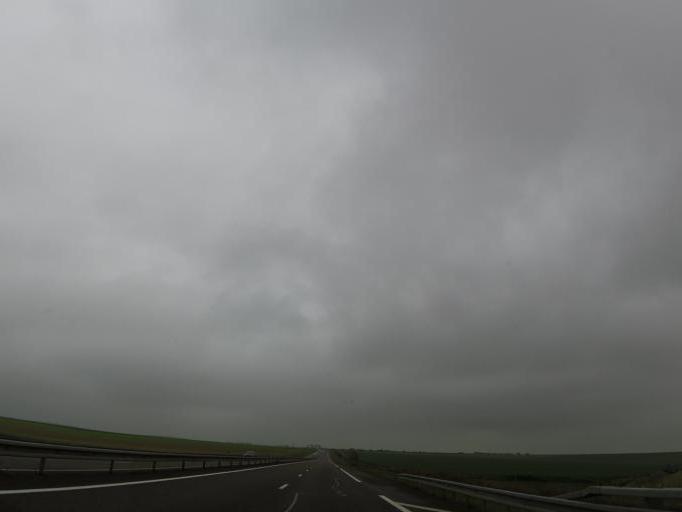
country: FR
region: Champagne-Ardenne
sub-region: Departement de la Marne
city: Courtisols
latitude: 49.0361
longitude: 4.5889
